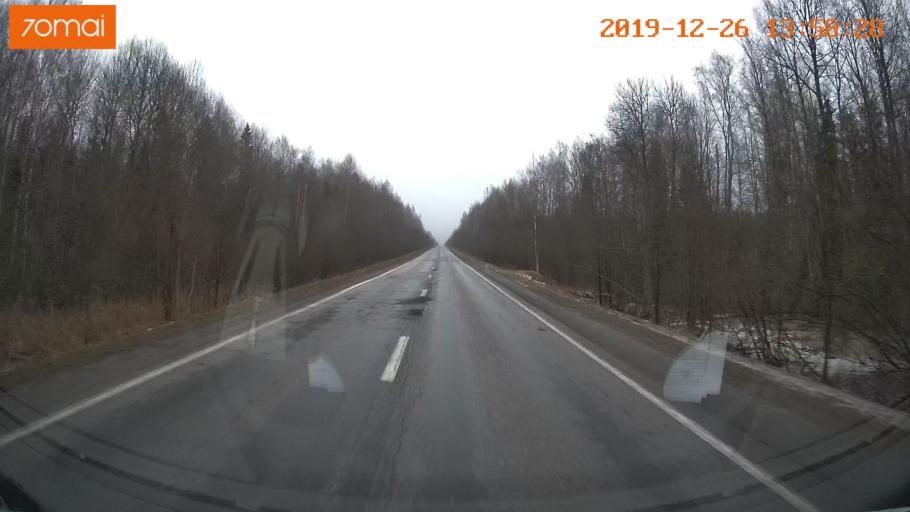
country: RU
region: Jaroslavl
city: Poshekhon'ye
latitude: 58.5739
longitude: 38.7013
